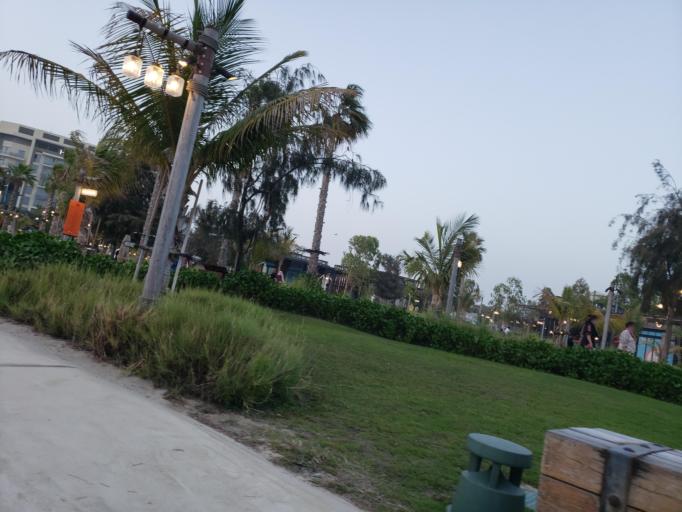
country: AE
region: Ash Shariqah
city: Sharjah
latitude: 25.2326
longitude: 55.2601
